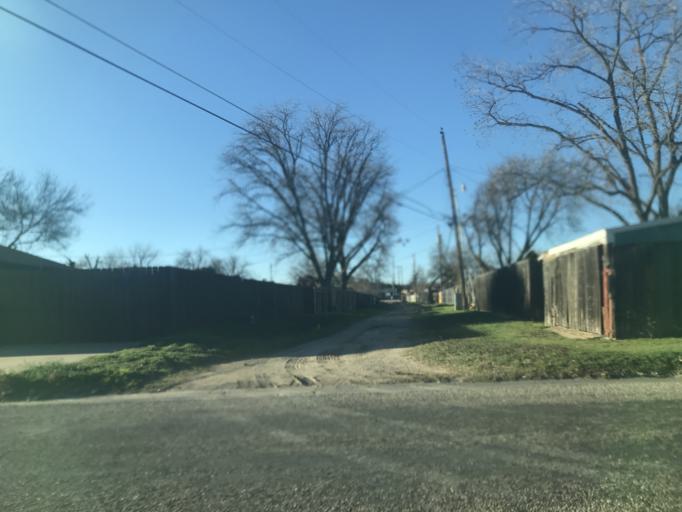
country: US
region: Texas
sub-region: Tom Green County
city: San Angelo
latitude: 31.4399
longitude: -100.4857
